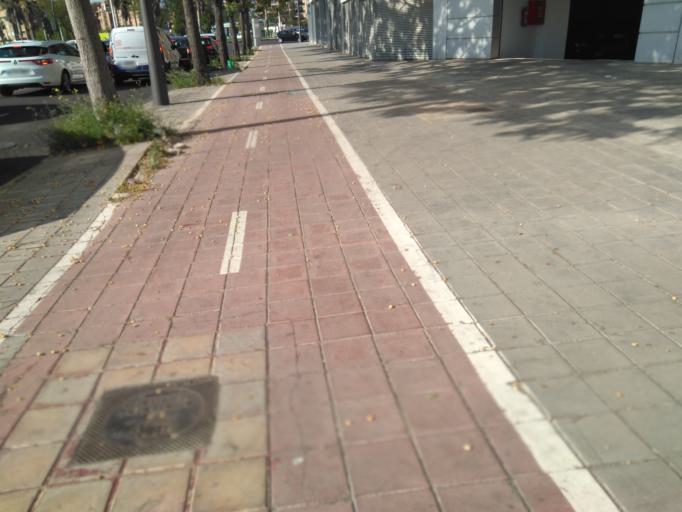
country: ES
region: Valencia
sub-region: Provincia de Valencia
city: Mislata
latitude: 39.4867
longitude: -0.4051
